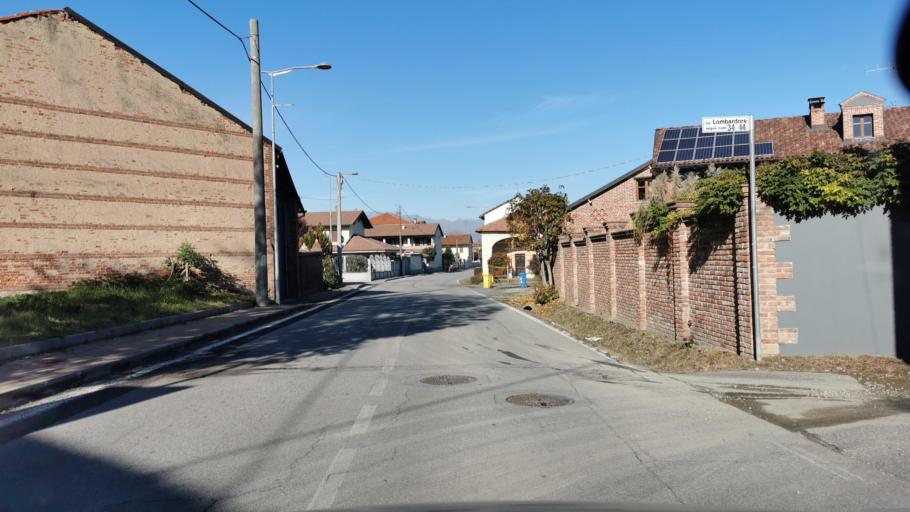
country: IT
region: Piedmont
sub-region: Provincia di Torino
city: Volpiano
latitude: 45.2062
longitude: 7.7746
